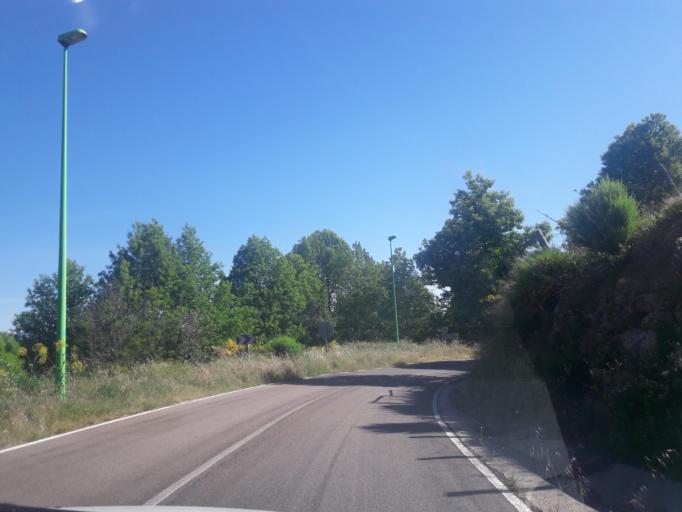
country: ES
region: Castille and Leon
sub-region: Provincia de Salamanca
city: Montemayor del Rio
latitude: 40.3274
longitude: -5.9175
